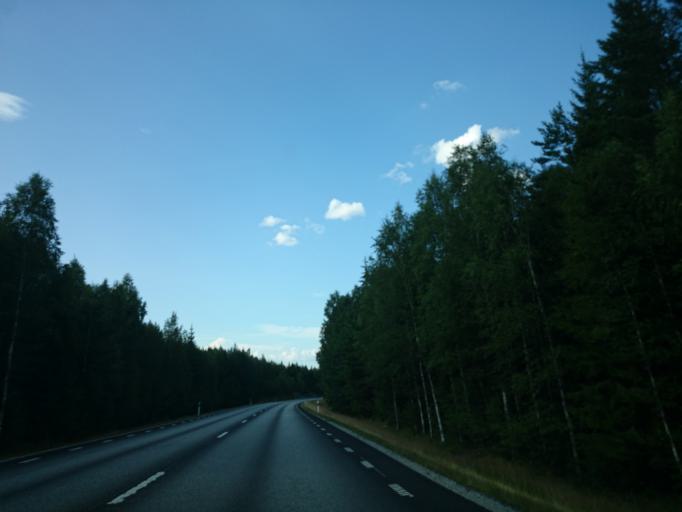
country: SE
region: OErebro
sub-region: Lindesbergs Kommun
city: Lindesberg
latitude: 59.7416
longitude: 15.4295
